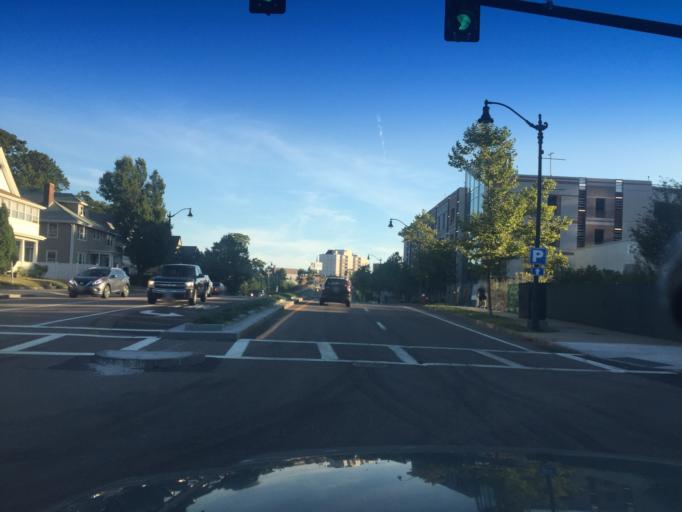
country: US
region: Massachusetts
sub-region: Norfolk County
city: Quincy
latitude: 42.2491
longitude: -70.9992
